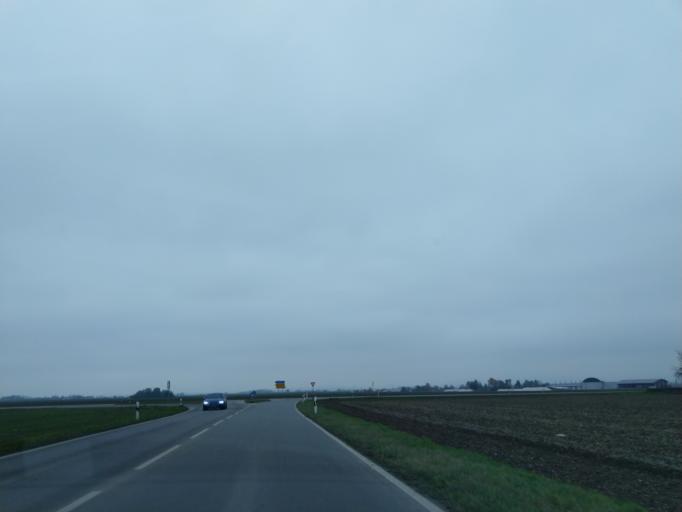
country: DE
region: Bavaria
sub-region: Lower Bavaria
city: Plattling
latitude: 48.8029
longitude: 12.8489
